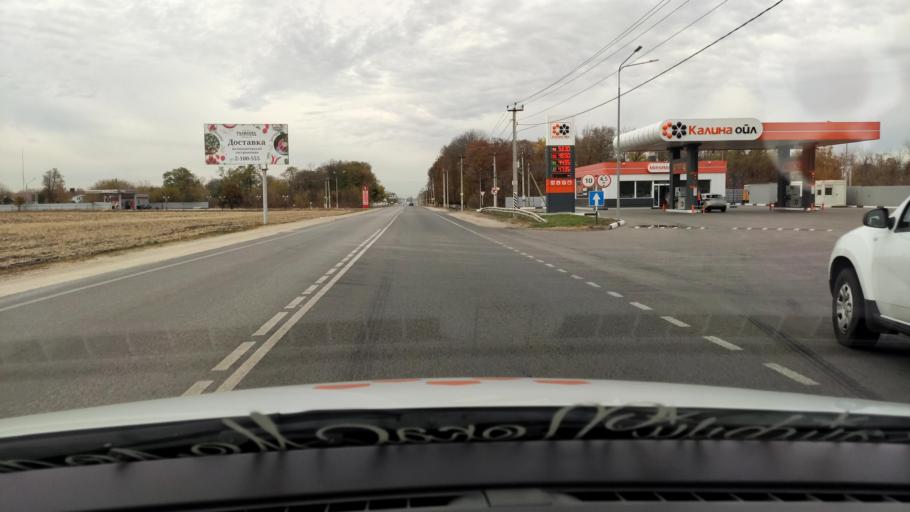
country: RU
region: Voronezj
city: Ramon'
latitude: 51.9256
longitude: 39.2588
